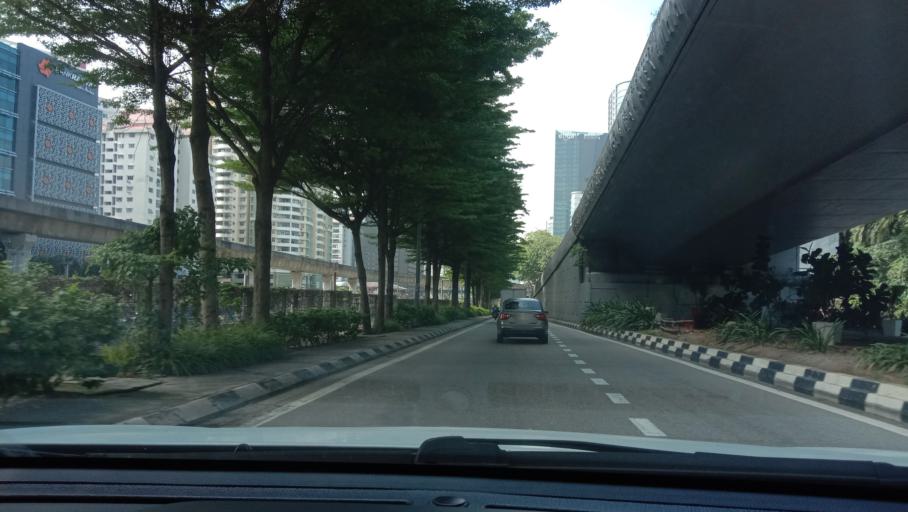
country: MY
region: Kuala Lumpur
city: Kuala Lumpur
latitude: 3.1316
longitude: 101.6823
